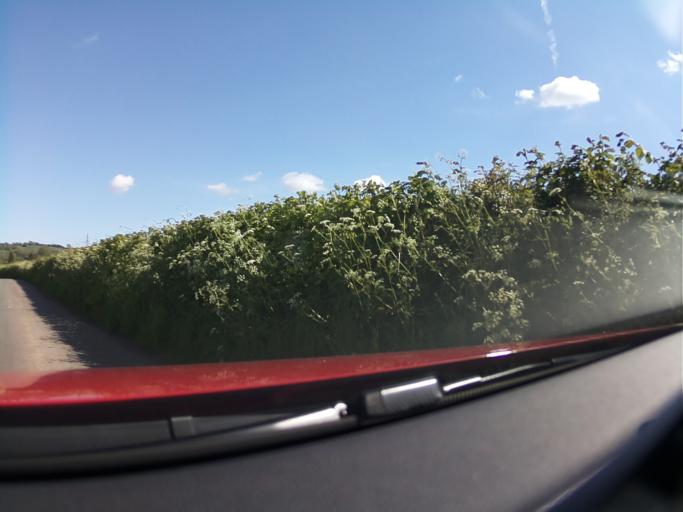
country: GB
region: Wales
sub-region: Caerphilly County Borough
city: Risca
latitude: 51.5684
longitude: -3.1019
